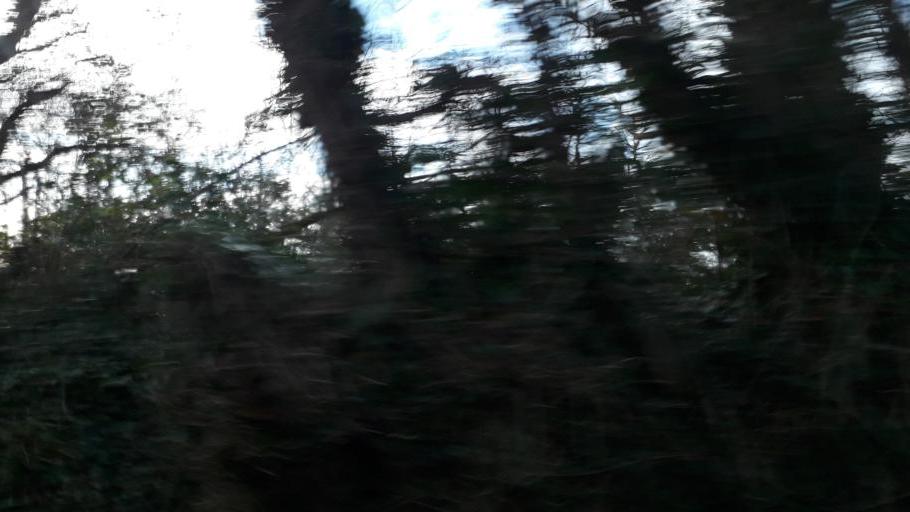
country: IE
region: Leinster
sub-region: Fingal County
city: Skerries
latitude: 53.5714
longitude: -6.1322
